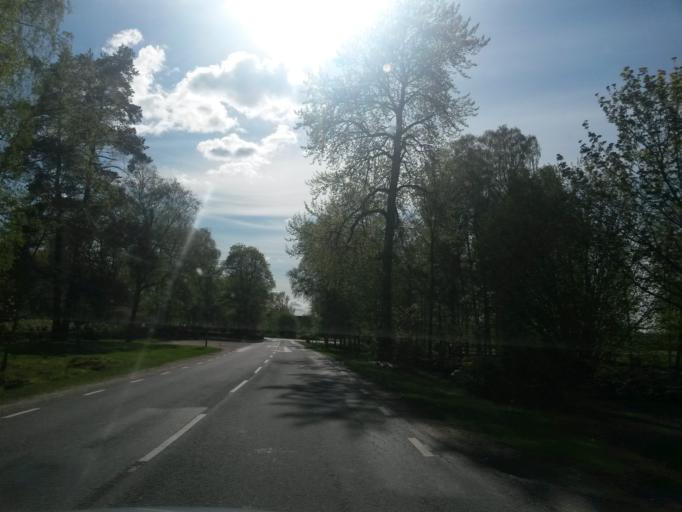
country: SE
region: Vaestra Goetaland
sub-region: Herrljunga Kommun
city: Herrljunga
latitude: 57.9498
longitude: 13.0105
